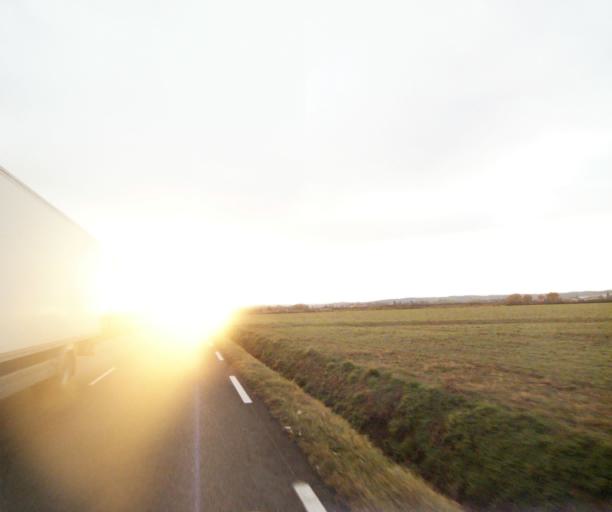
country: FR
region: Rhone-Alpes
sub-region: Departement de la Loire
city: Sury-le-Comtal
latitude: 45.5490
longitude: 4.1669
